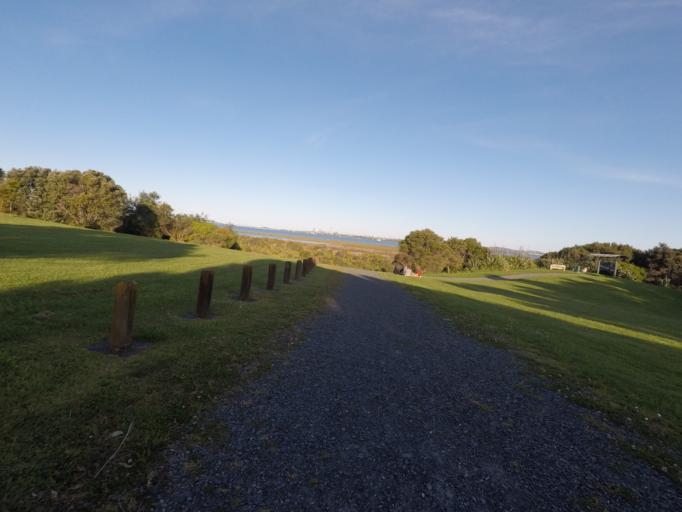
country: NZ
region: Auckland
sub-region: Auckland
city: Rosebank
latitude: -36.8478
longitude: 174.6535
